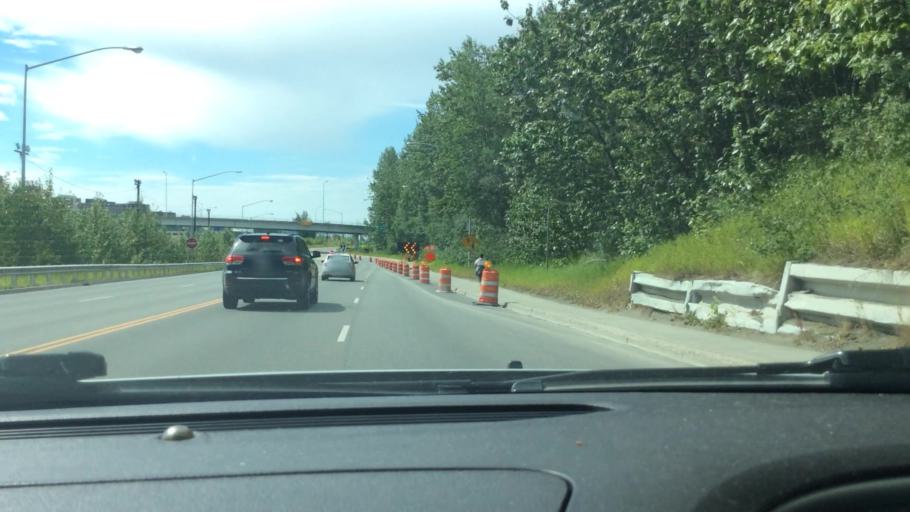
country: US
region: Alaska
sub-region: Anchorage Municipality
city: Anchorage
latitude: 61.2280
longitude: -149.8809
